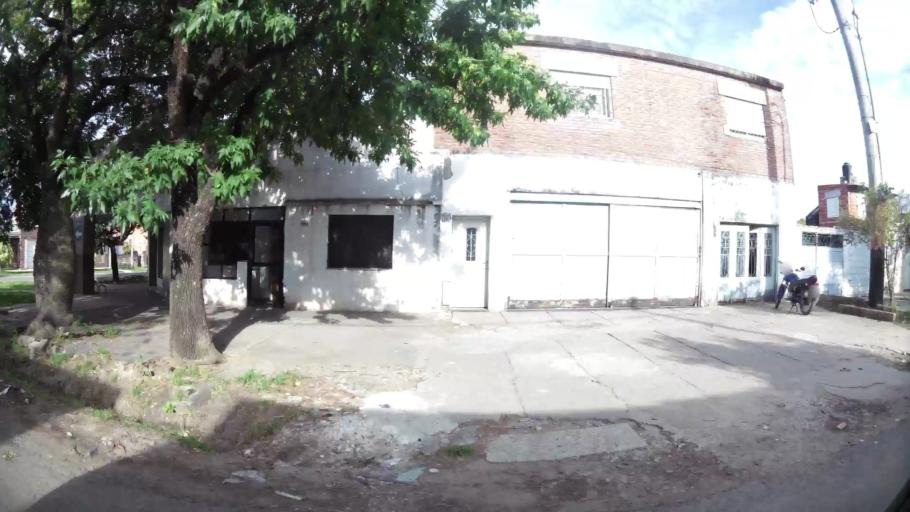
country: AR
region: Santa Fe
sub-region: Departamento de Rosario
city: Rosario
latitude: -32.9768
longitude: -60.6873
